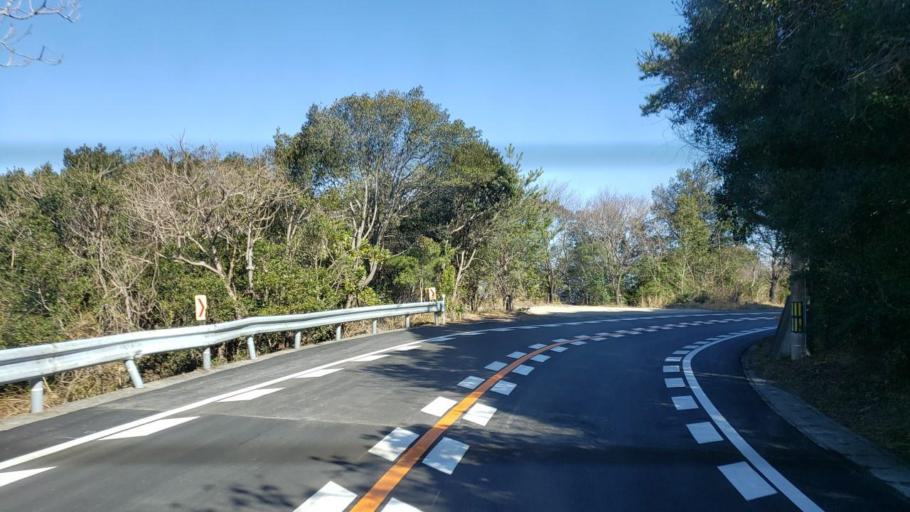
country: JP
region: Tokushima
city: Narutocho-mitsuishi
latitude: 34.2292
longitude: 134.6221
